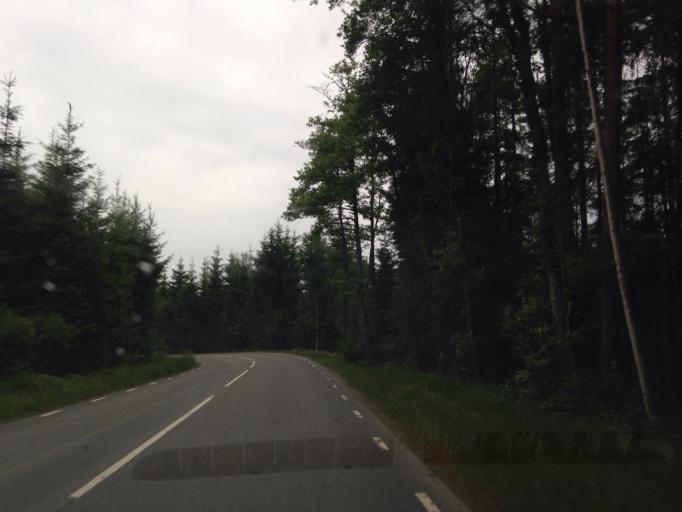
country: SE
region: Vaestra Goetaland
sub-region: Lerums Kommun
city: Lerum
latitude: 57.6826
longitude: 12.3226
